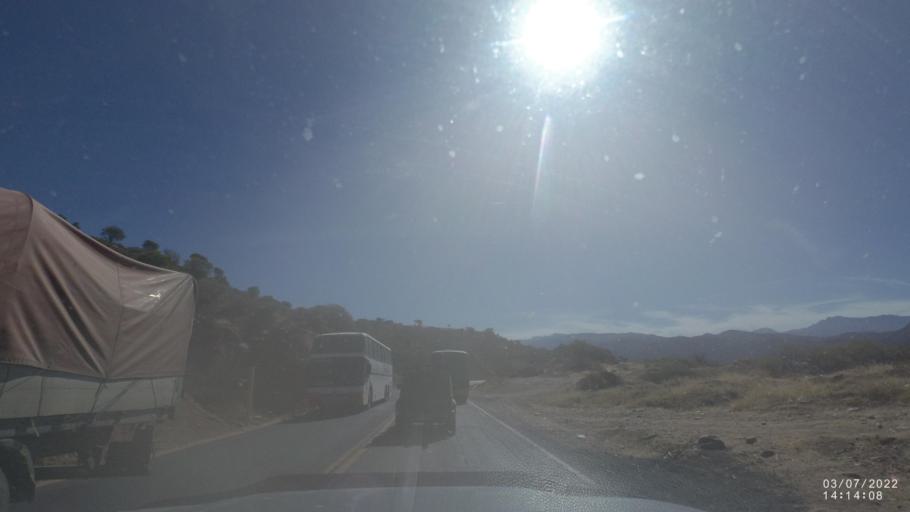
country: BO
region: Cochabamba
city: Sipe Sipe
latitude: -17.5915
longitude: -66.3468
